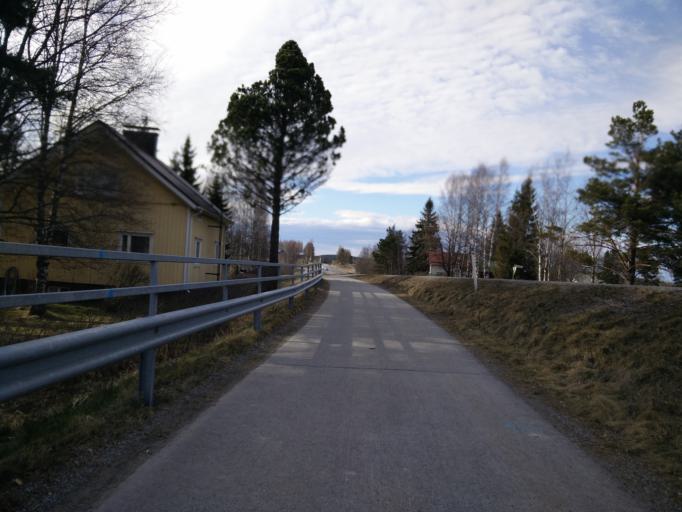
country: FI
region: Pirkanmaa
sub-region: Tampere
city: Orivesi
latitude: 61.7058
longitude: 24.3365
